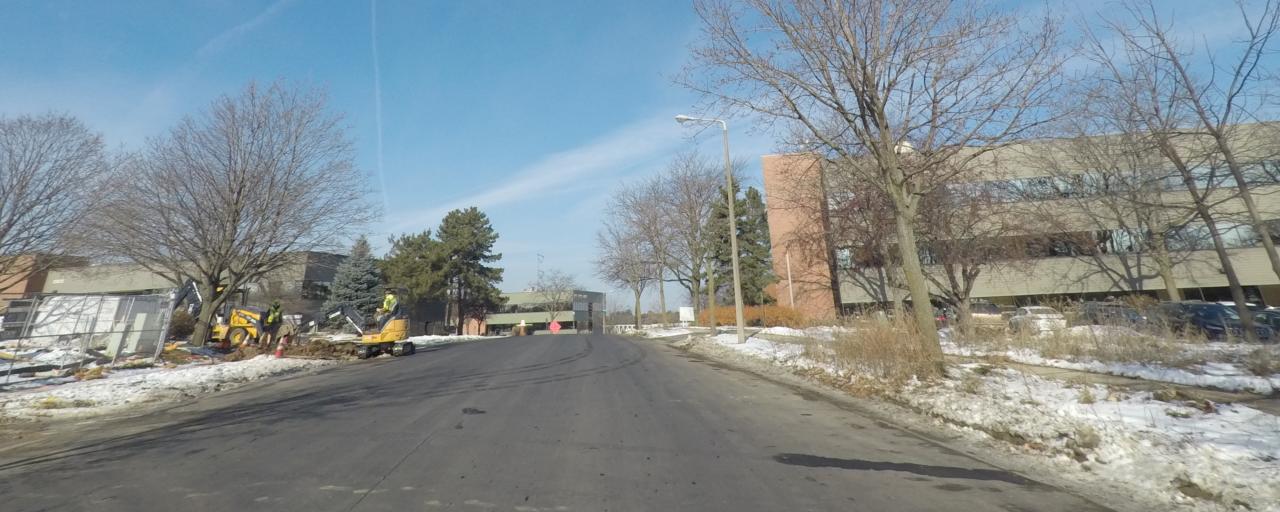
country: US
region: Wisconsin
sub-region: Dane County
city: Madison
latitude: 43.0318
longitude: -89.4147
